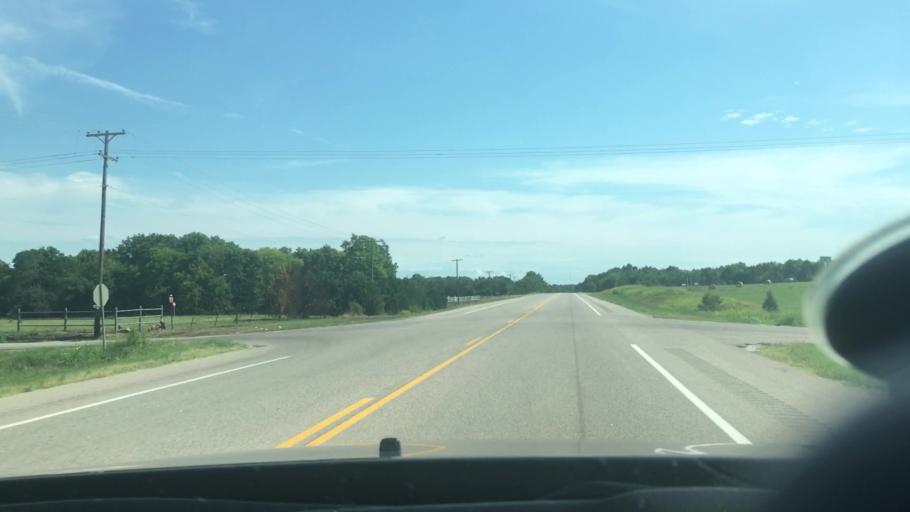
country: US
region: Oklahoma
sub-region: Seminole County
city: Konawa
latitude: 34.9712
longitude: -96.6790
